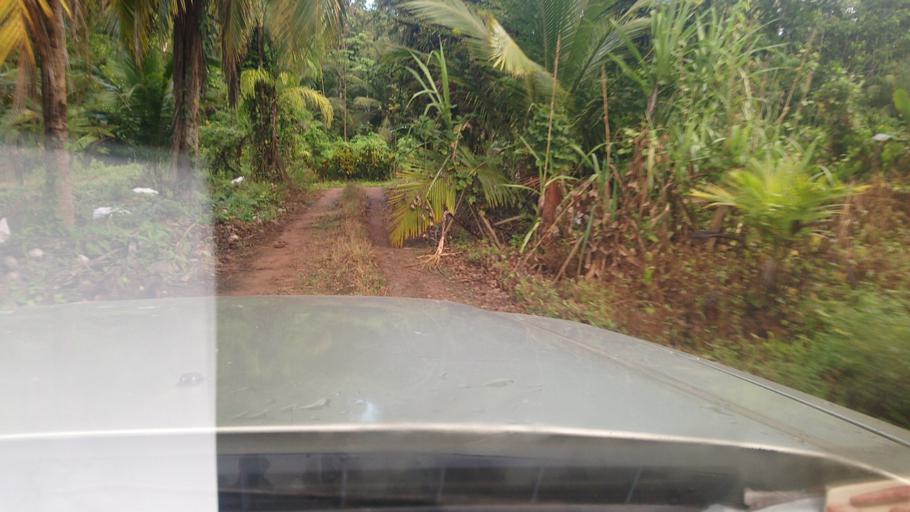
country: TT
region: Couva-Tabaquite-Talparo
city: Tabaquite
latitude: 10.4813
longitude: -61.2081
